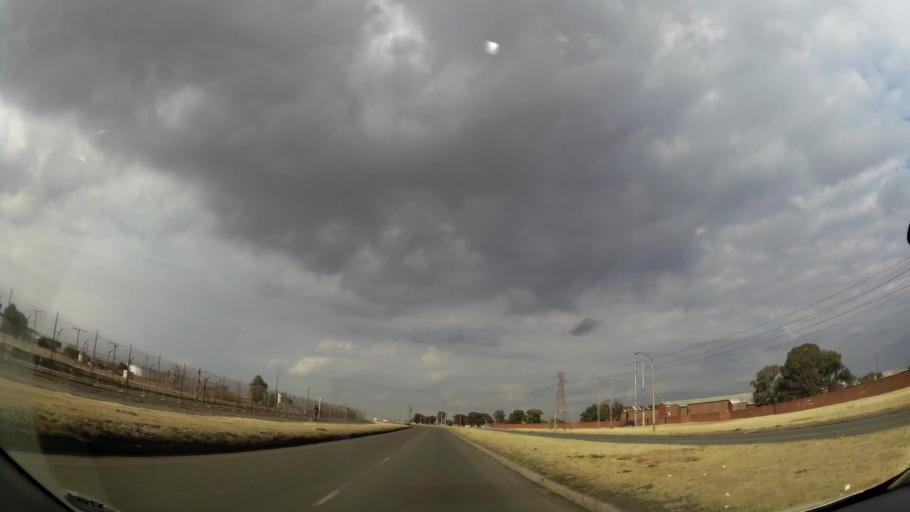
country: ZA
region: Orange Free State
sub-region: Fezile Dabi District Municipality
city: Sasolburg
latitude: -26.8350
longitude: 27.8467
